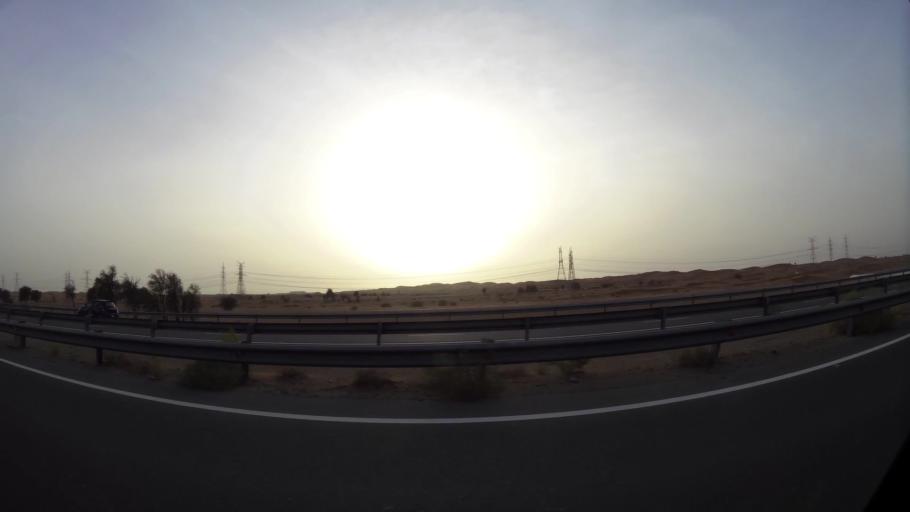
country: OM
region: Al Buraimi
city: Al Buraymi
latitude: 24.3035
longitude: 55.7437
